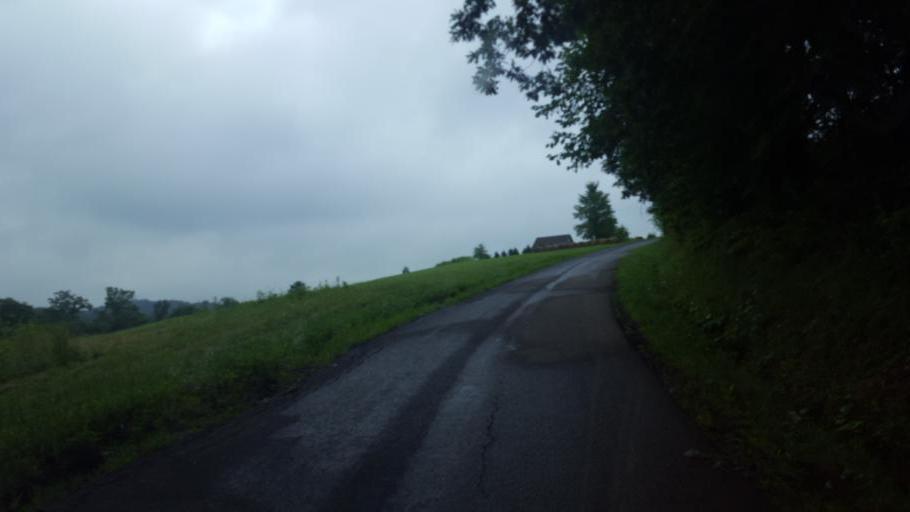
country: US
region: Ohio
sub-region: Columbiana County
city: Salineville
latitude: 40.5753
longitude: -80.8614
